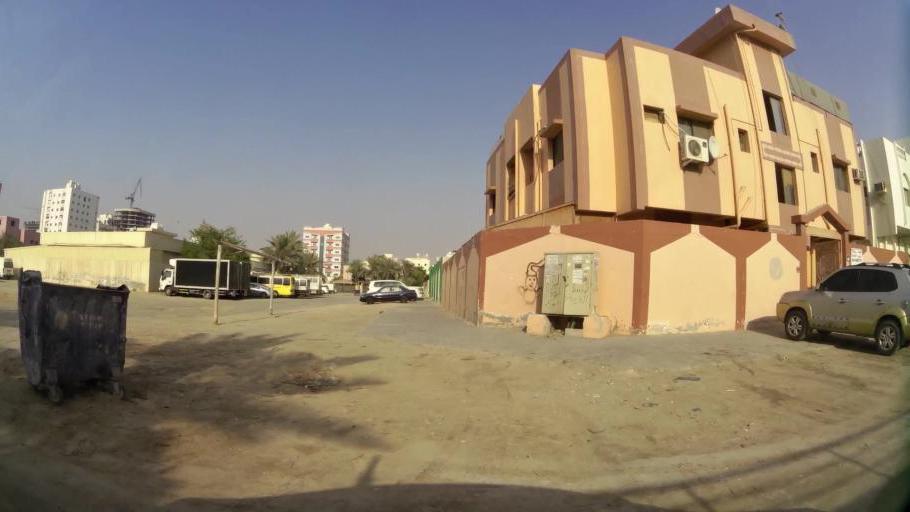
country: AE
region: Ajman
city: Ajman
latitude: 25.3863
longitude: 55.4434
